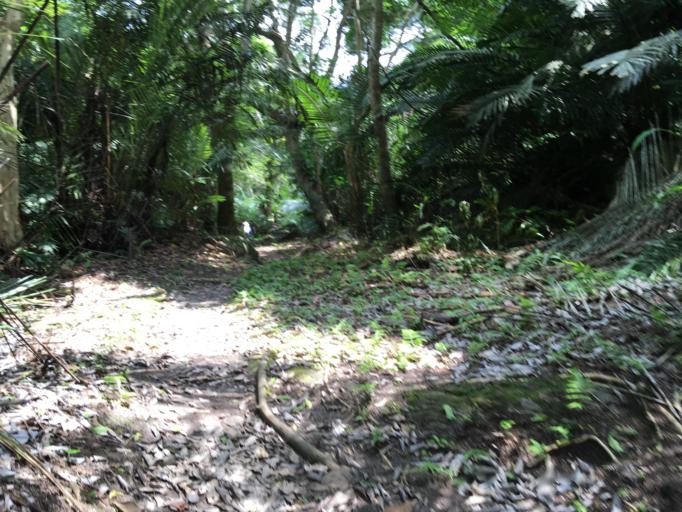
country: TW
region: Taiwan
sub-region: Yilan
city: Yilan
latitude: 24.4290
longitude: 121.6932
